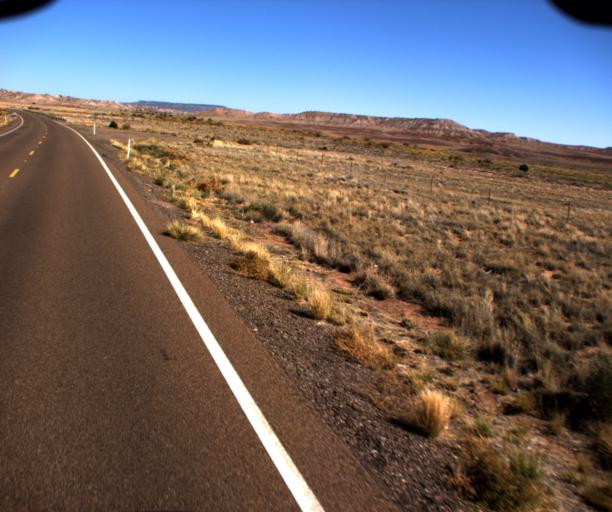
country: US
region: Arizona
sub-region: Navajo County
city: Joseph City
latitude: 35.1692
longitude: -110.4478
